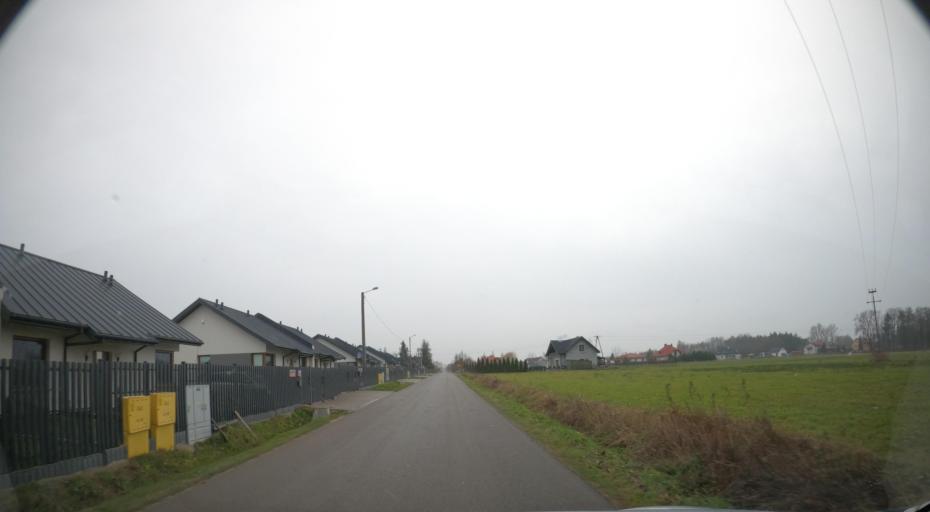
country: PL
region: Masovian Voivodeship
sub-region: Powiat radomski
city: Jastrzebia
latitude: 51.4246
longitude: 21.2374
